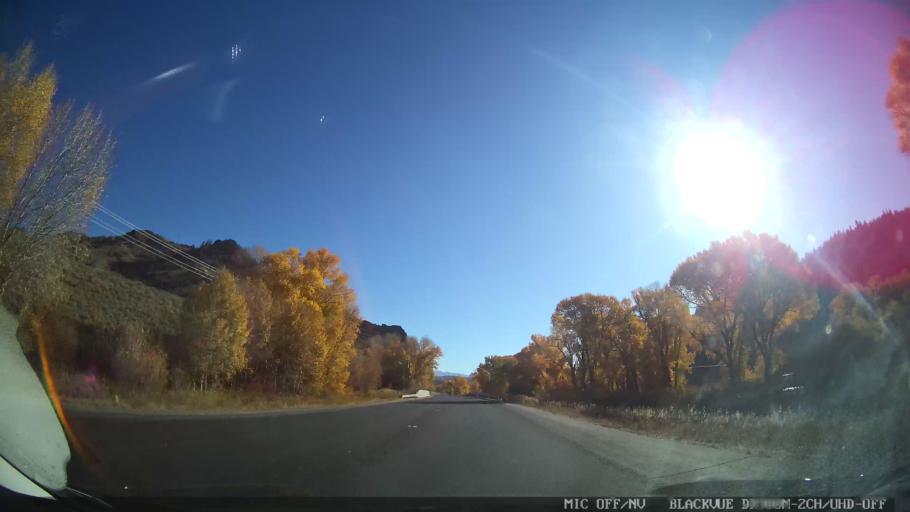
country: US
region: Colorado
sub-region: Grand County
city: Granby
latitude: 40.1085
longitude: -106.0064
